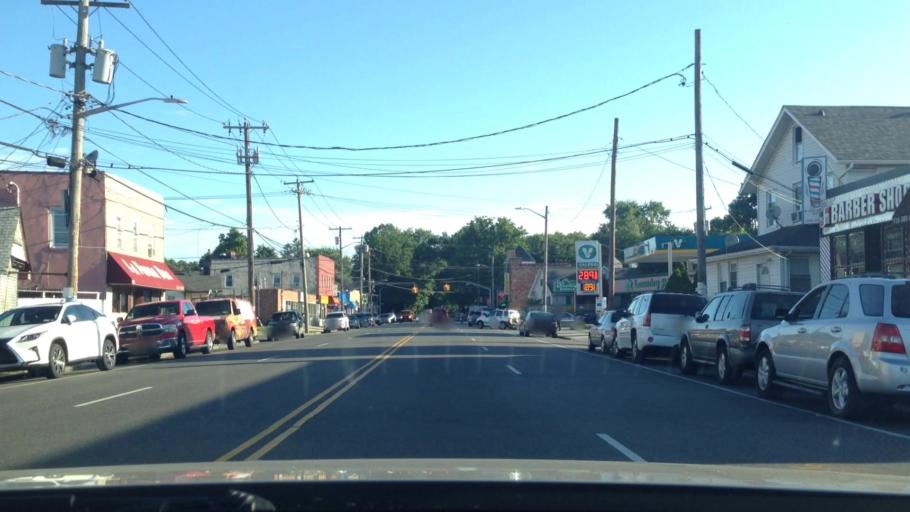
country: US
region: New York
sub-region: Nassau County
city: Hempstead
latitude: 40.7177
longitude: -73.6207
